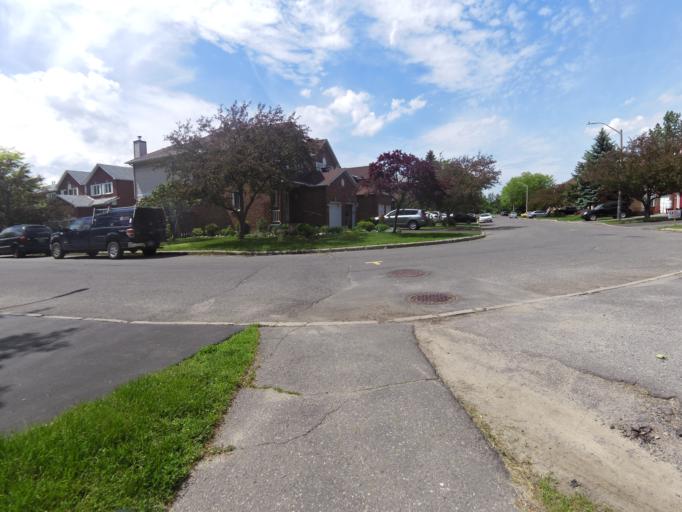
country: CA
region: Ontario
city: Ottawa
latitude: 45.3603
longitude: -75.6372
